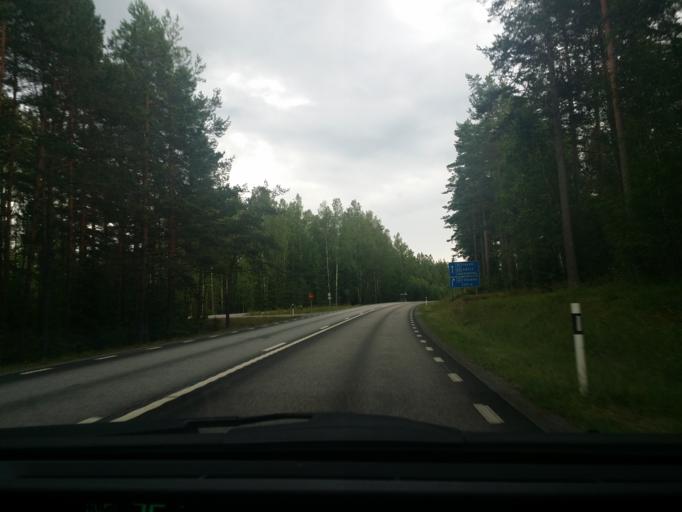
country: SE
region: OErebro
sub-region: Nora Kommun
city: Nora
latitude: 59.4741
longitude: 15.1247
